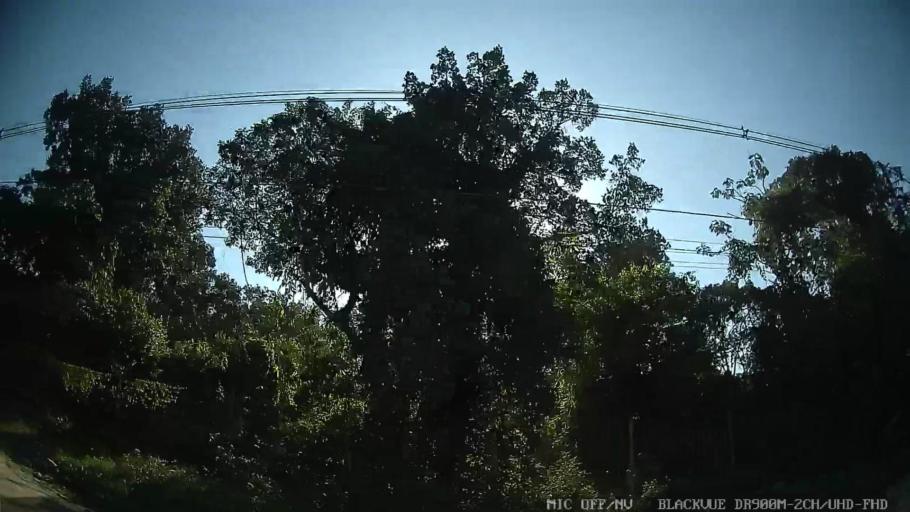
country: BR
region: Sao Paulo
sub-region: Guaruja
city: Guaruja
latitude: -23.9699
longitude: -46.2152
